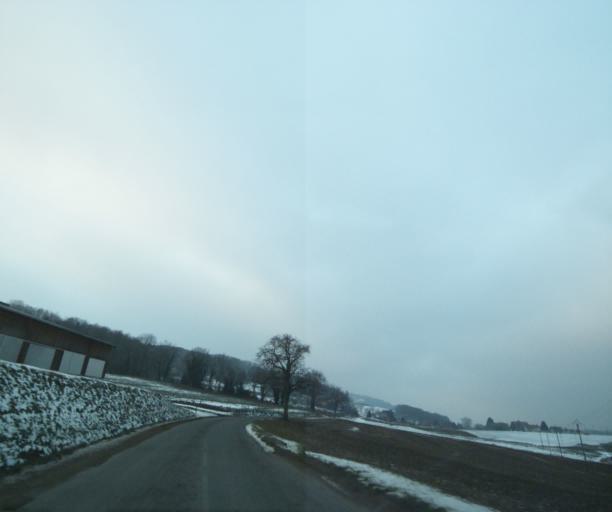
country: FR
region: Rhone-Alpes
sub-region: Departement de la Haute-Savoie
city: Reignier-Esery
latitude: 46.1454
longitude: 6.2487
